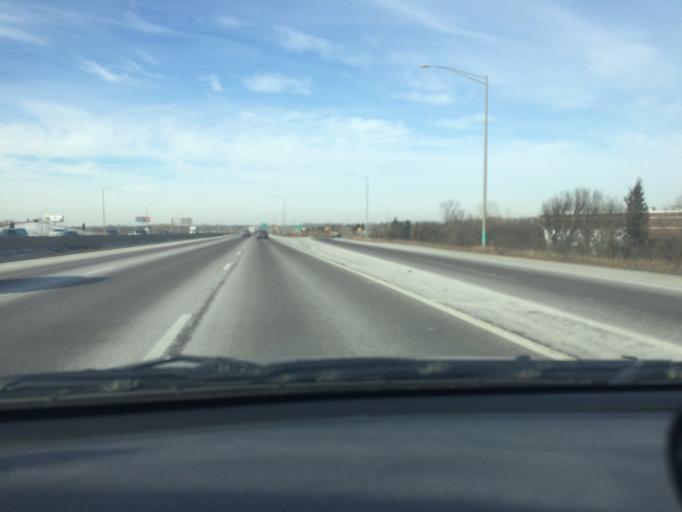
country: US
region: Illinois
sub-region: DuPage County
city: Addison
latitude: 41.9271
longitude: -87.9615
